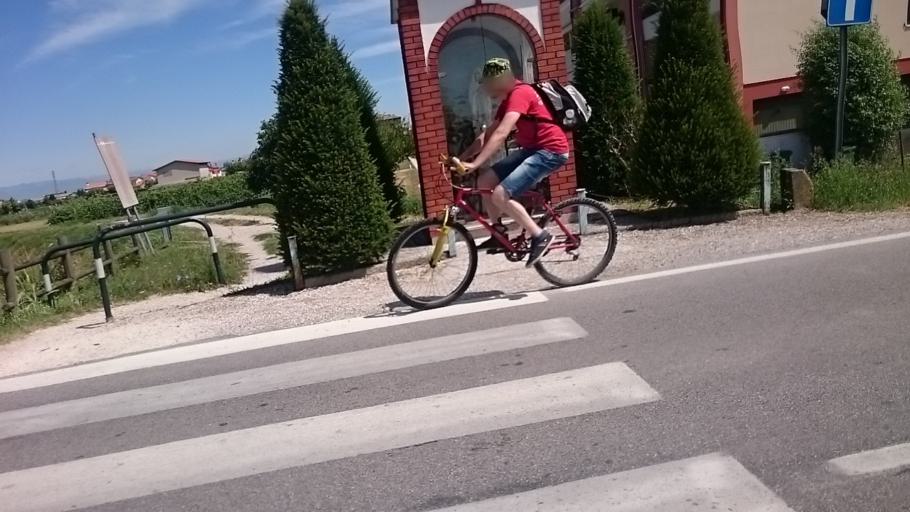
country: IT
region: Veneto
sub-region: Provincia di Padova
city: Pionca
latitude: 45.4660
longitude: 11.9594
